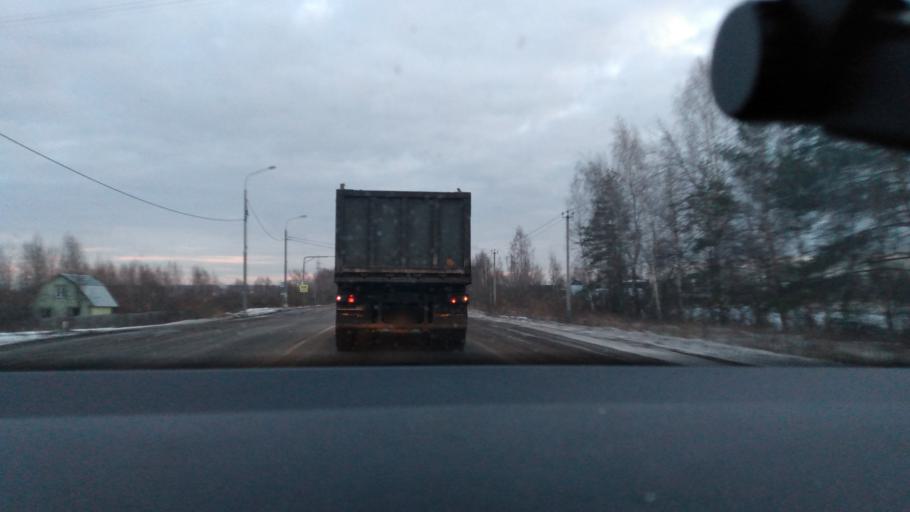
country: RU
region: Moskovskaya
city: Yegor'yevsk
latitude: 55.4097
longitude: 39.0512
